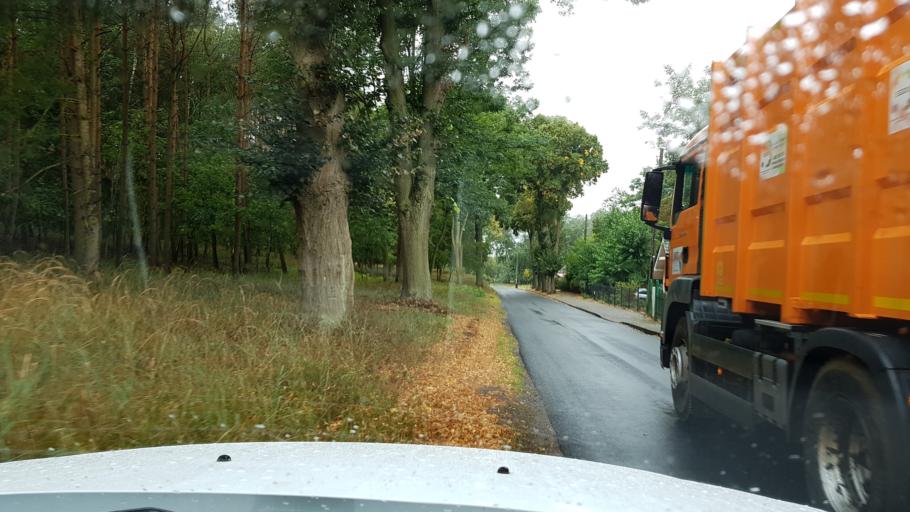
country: DE
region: Brandenburg
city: Schoneberg
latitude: 52.9413
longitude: 14.1528
